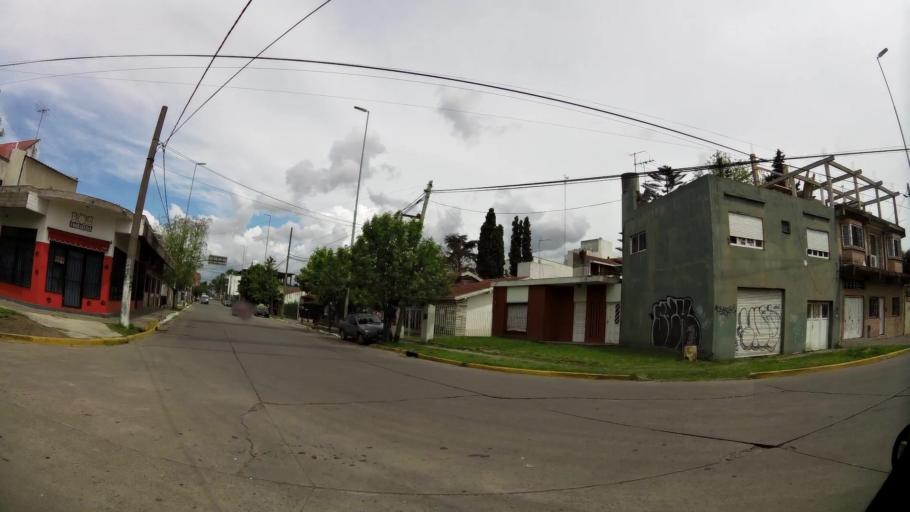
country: AR
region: Buenos Aires
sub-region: Partido de Quilmes
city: Quilmes
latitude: -34.7773
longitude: -58.2631
